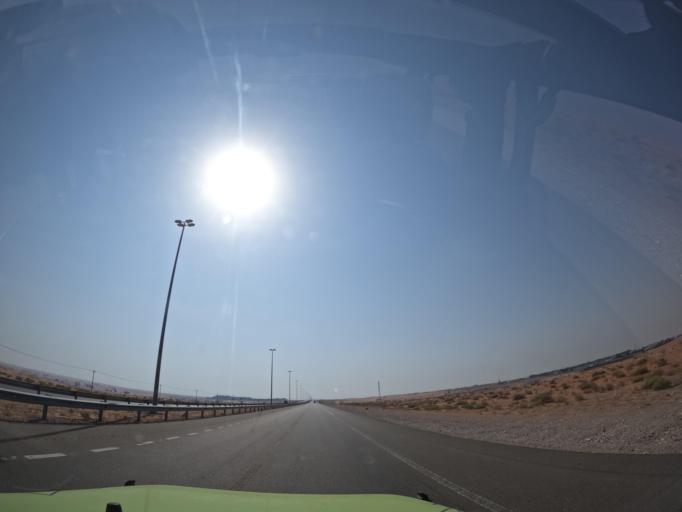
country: OM
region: Al Buraimi
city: Al Buraymi
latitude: 24.4247
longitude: 55.6845
